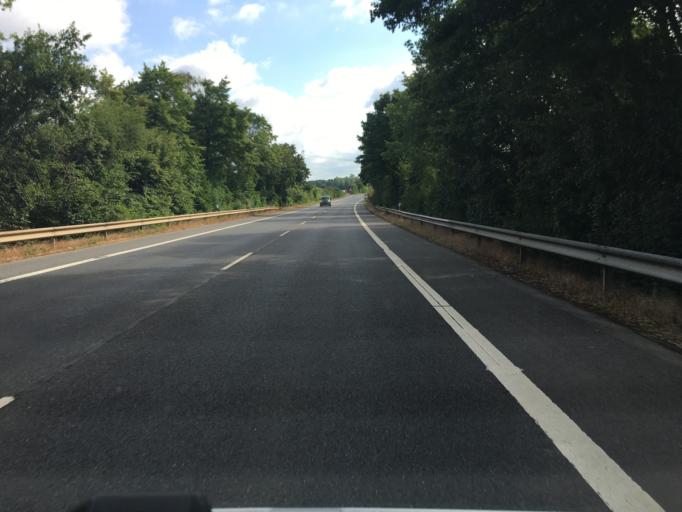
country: DE
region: North Rhine-Westphalia
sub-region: Regierungsbezirk Dusseldorf
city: Dormagen
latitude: 51.1057
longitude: 6.8099
